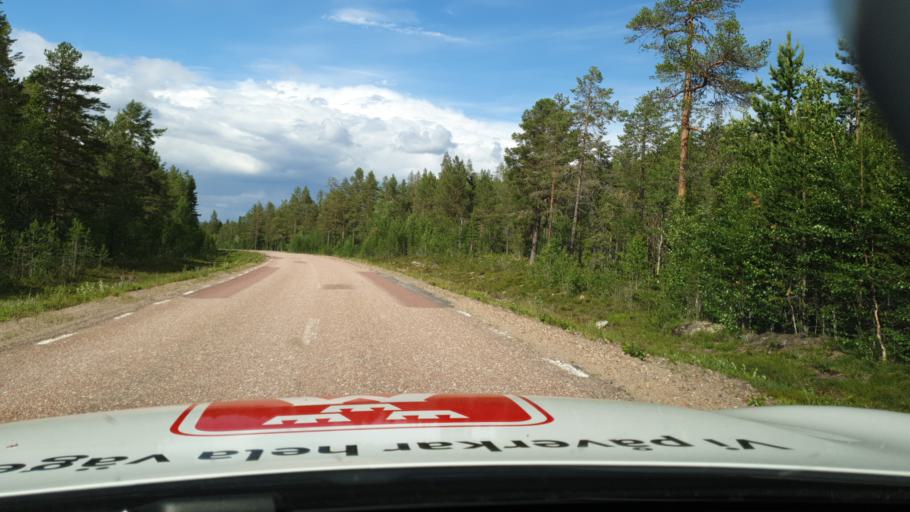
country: SE
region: Dalarna
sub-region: Alvdalens Kommun
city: AElvdalen
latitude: 61.7708
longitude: 13.4822
